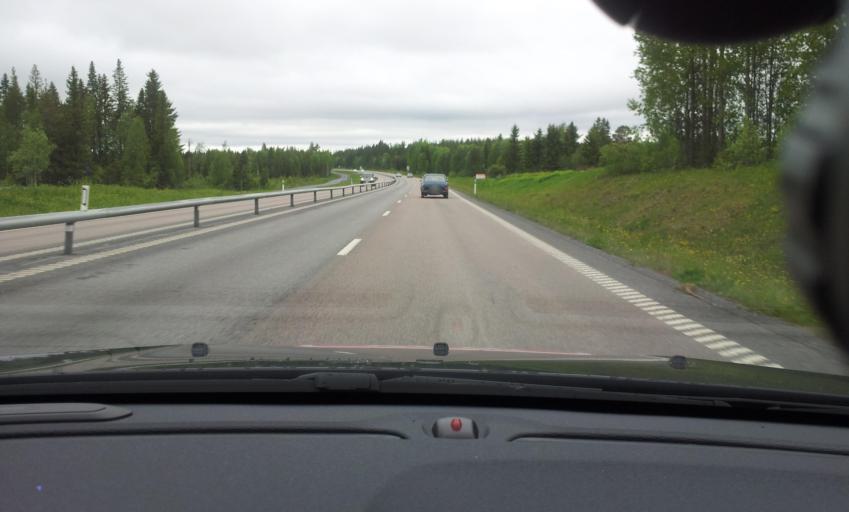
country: SE
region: Jaemtland
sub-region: Krokoms Kommun
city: Krokom
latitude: 63.2706
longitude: 14.5357
